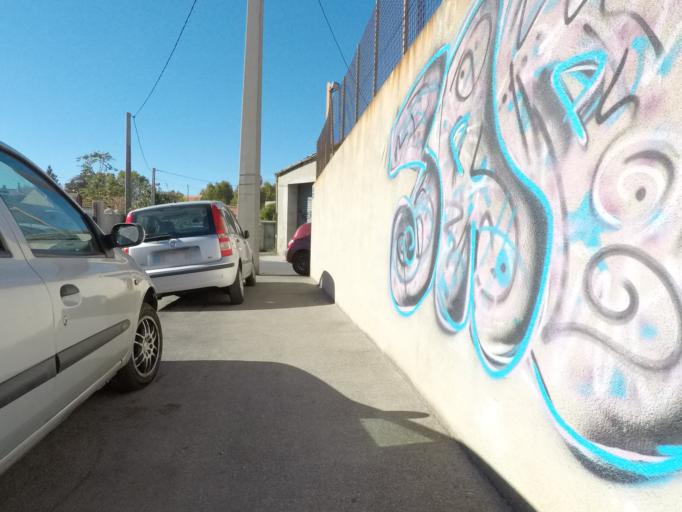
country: FR
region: Provence-Alpes-Cote d'Azur
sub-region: Departement des Bouches-du-Rhone
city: Marseille 10
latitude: 43.2765
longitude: 5.4120
